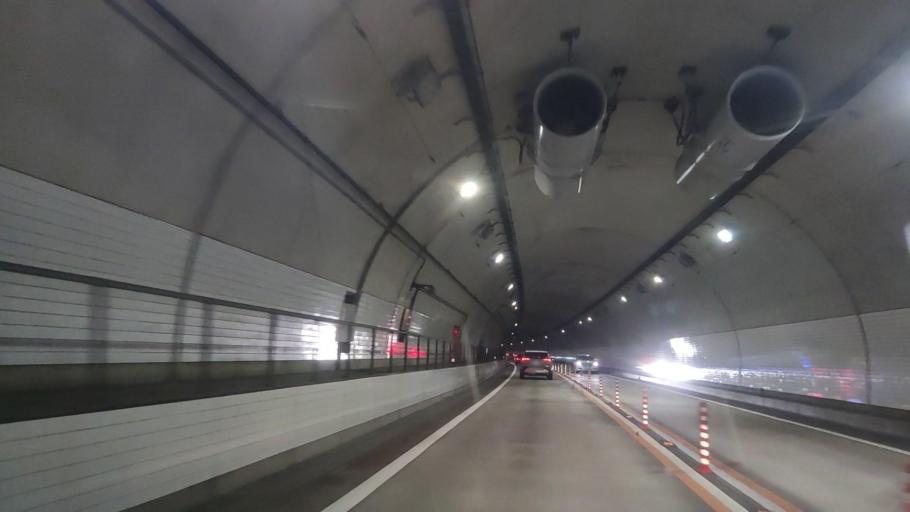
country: JP
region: Kyoto
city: Miyazu
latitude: 35.5652
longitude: 135.1209
